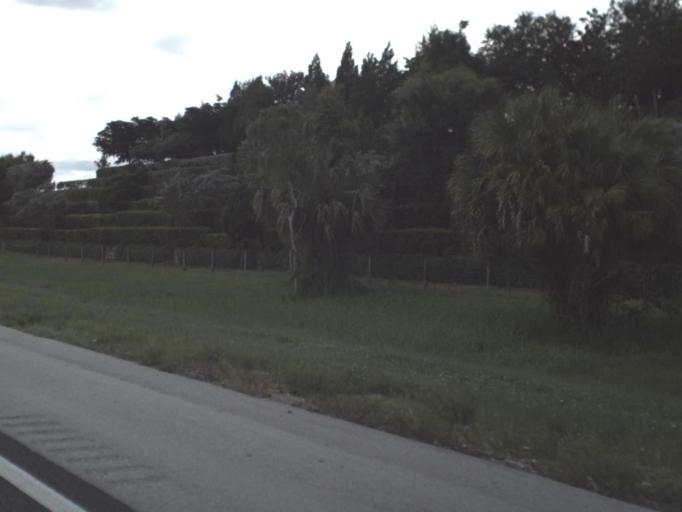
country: US
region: Florida
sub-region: Lee County
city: Bonita Springs
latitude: 26.3051
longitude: -81.7432
